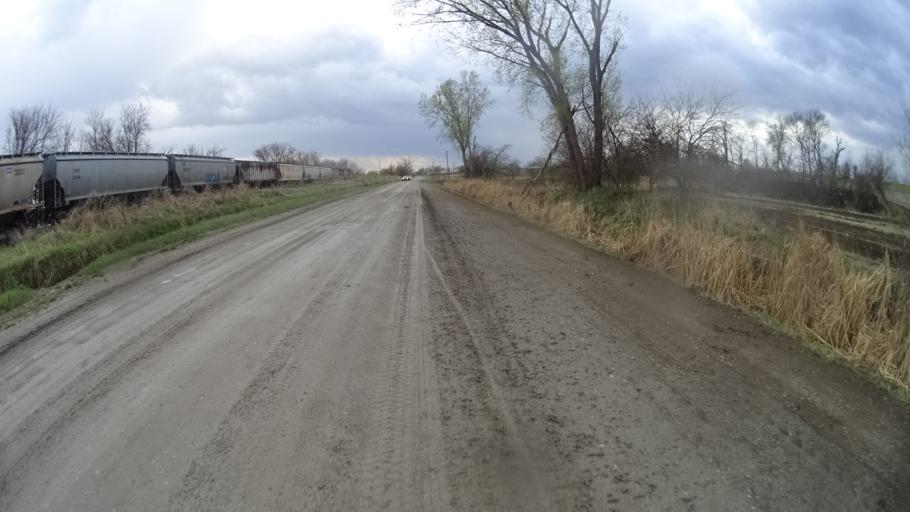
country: US
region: Nebraska
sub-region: Sarpy County
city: Offutt Air Force Base
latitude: 41.0793
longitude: -95.9197
